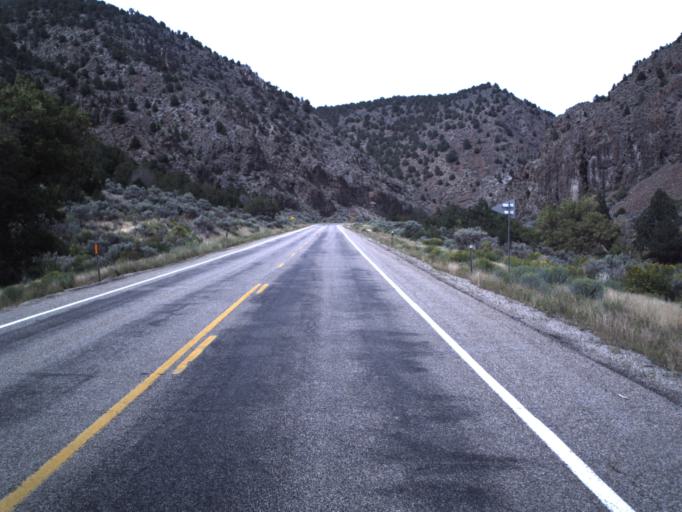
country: US
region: Utah
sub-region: Piute County
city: Junction
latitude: 38.1131
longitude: -112.3379
